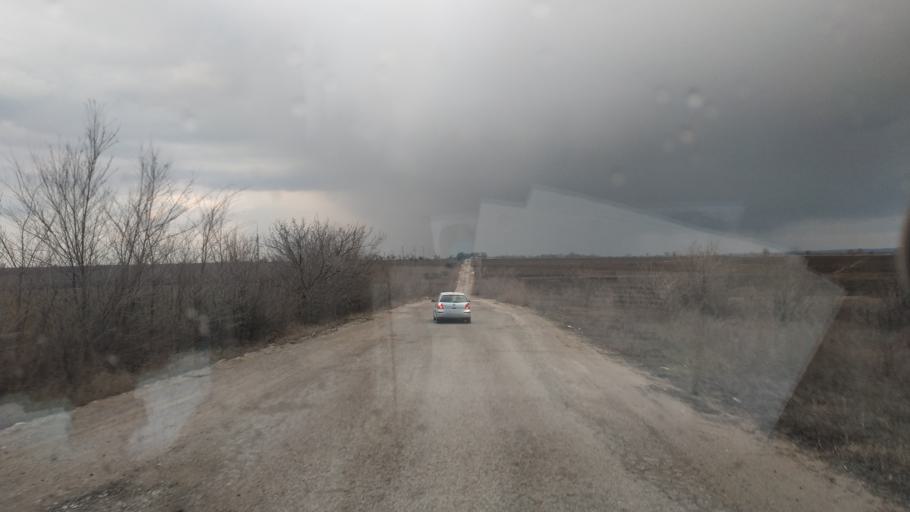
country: MD
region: Telenesti
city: Grigoriopol
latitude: 47.0589
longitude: 29.2961
